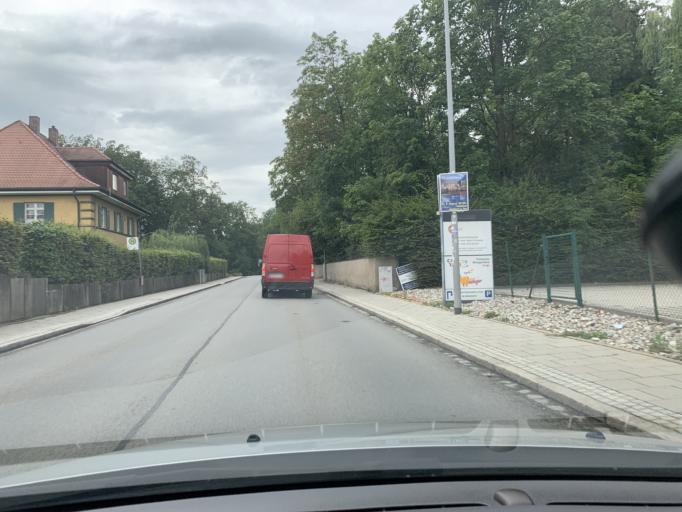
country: DE
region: Bavaria
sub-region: Upper Bavaria
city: Muehldorf
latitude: 48.2448
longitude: 12.5264
